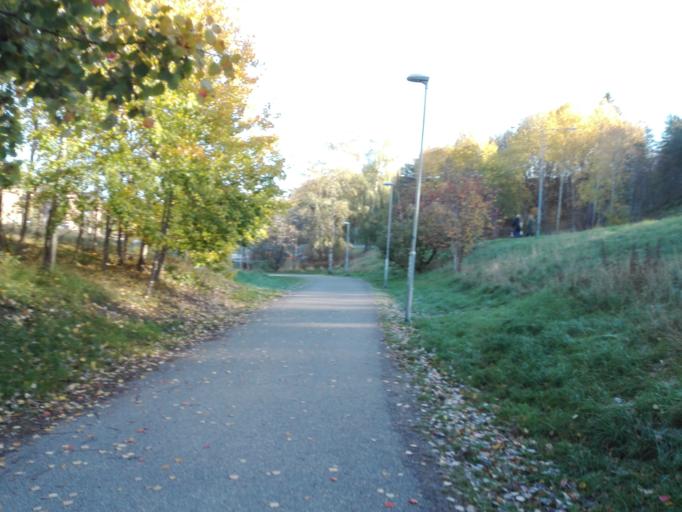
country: SE
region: Stockholm
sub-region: Nacka Kommun
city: Fisksatra
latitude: 59.2899
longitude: 18.2497
